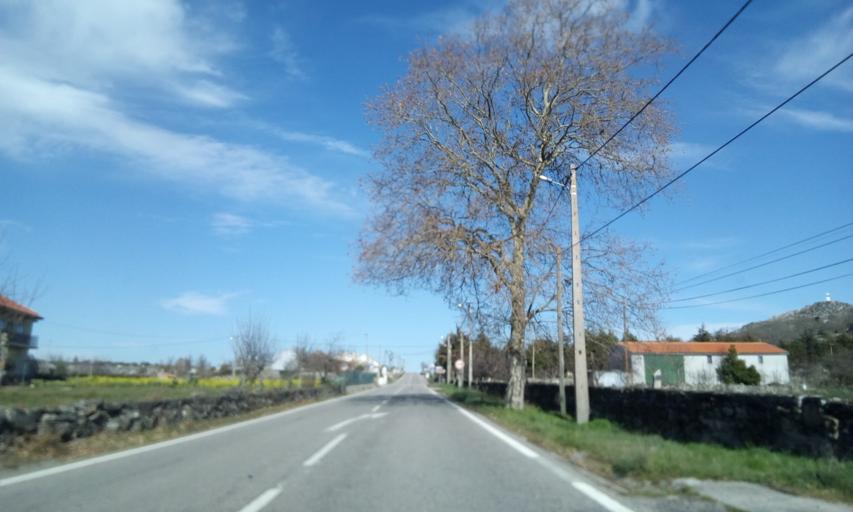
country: PT
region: Guarda
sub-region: Guarda
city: Sequeira
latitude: 40.5903
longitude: -7.1424
